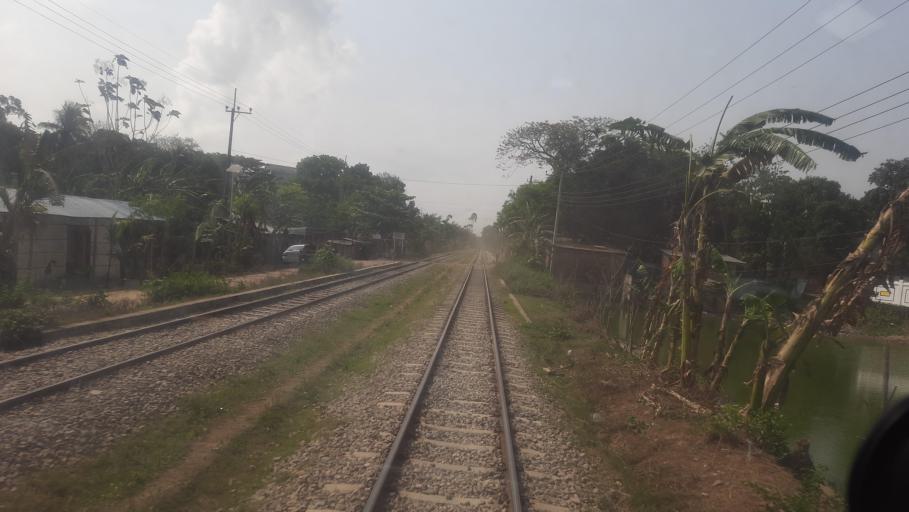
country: BD
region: Chittagong
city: Chittagong
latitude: 22.3837
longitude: 91.7689
